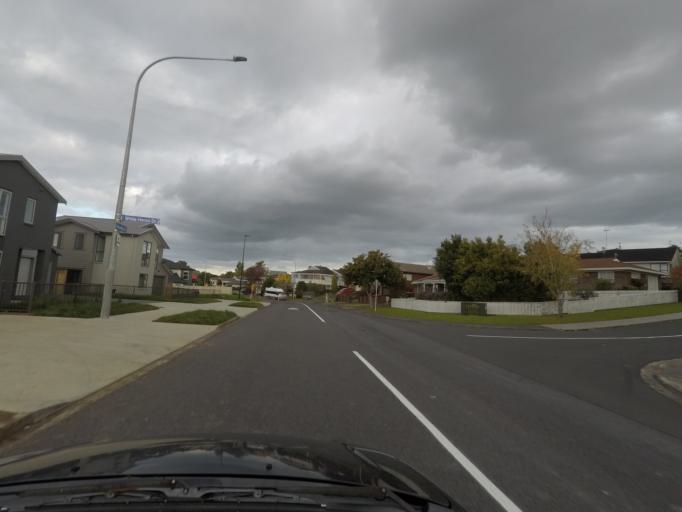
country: NZ
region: Auckland
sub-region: Auckland
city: Rosebank
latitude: -36.8281
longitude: 174.6246
